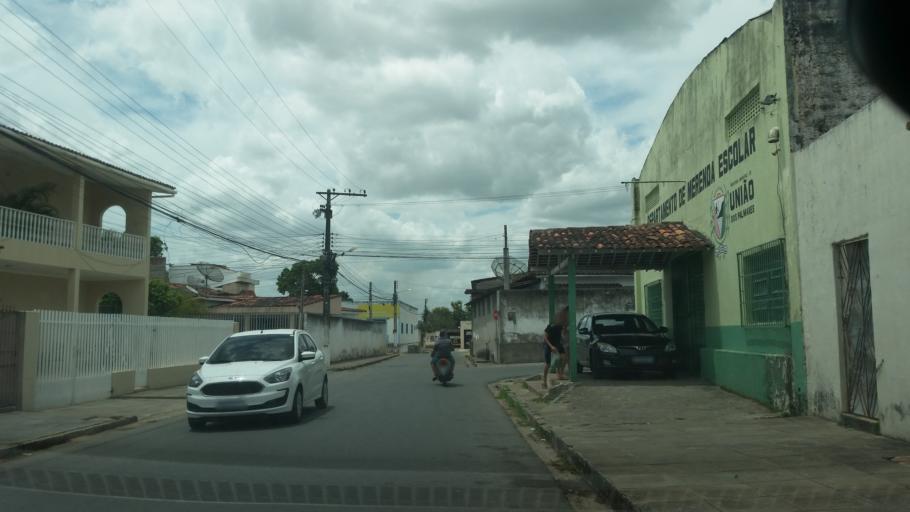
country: BR
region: Alagoas
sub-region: Uniao Dos Palmares
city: Uniao dos Palmares
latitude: -9.1606
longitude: -36.0348
